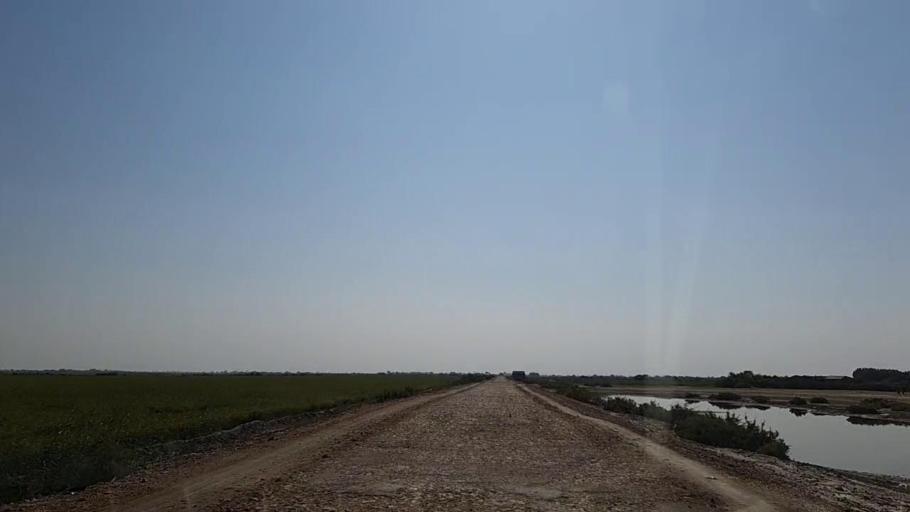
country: PK
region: Sindh
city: Chuhar Jamali
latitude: 24.4735
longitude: 68.0912
